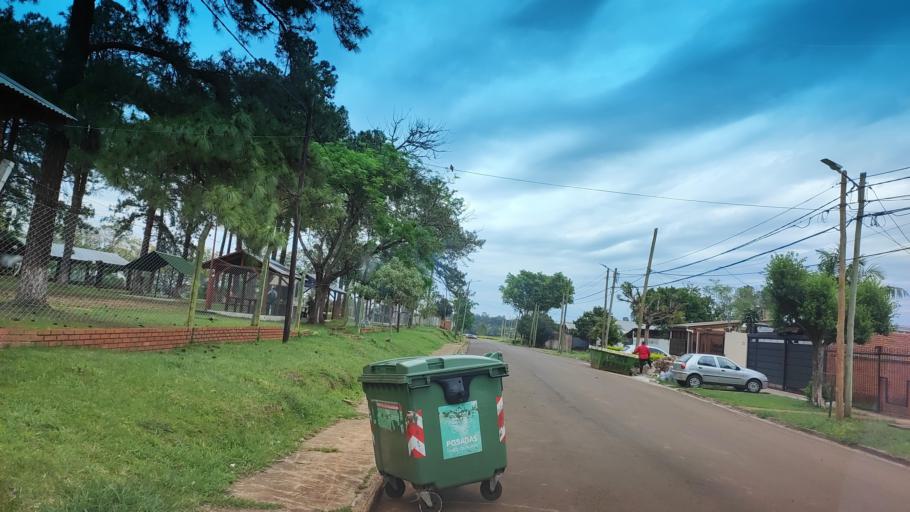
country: AR
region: Misiones
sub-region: Departamento de Capital
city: Posadas
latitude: -27.4043
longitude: -55.9507
